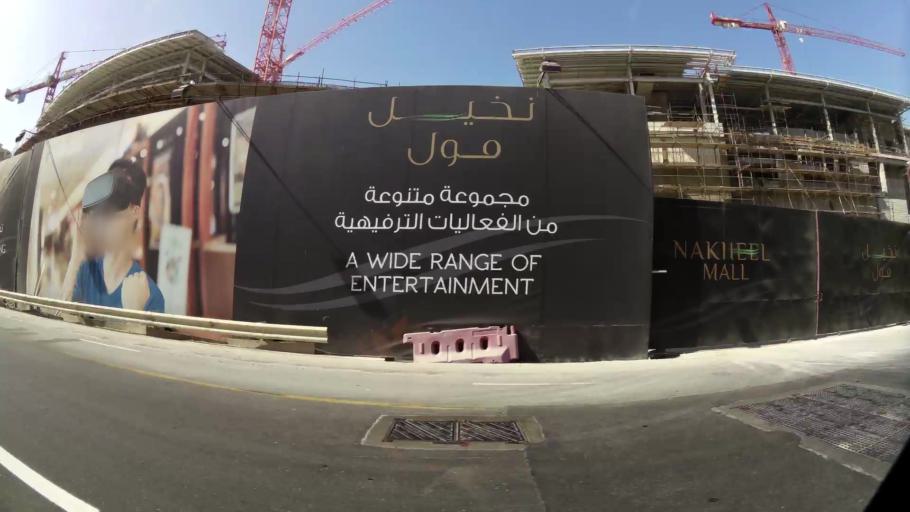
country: AE
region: Dubai
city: Dubai
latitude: 25.1132
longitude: 55.1378
